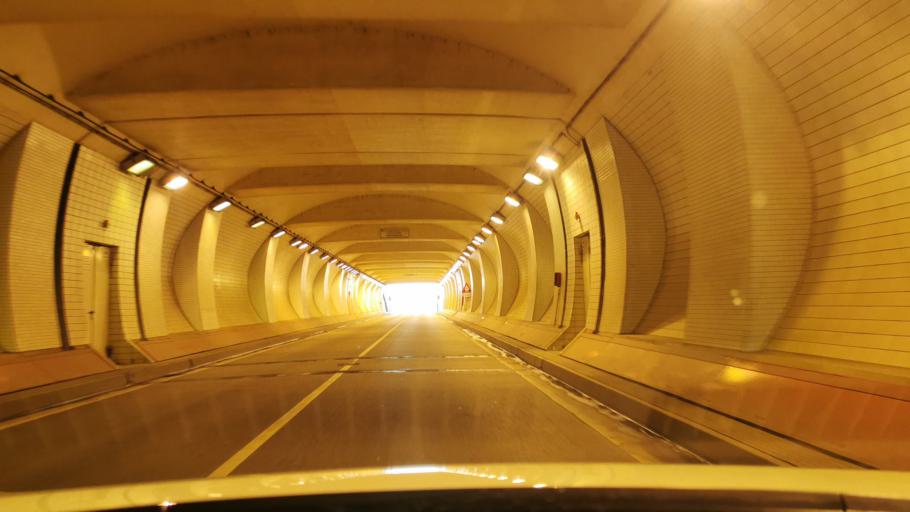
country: DE
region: Schleswig-Holstein
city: Wesselburenerkoog
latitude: 54.2646
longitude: 8.8455
